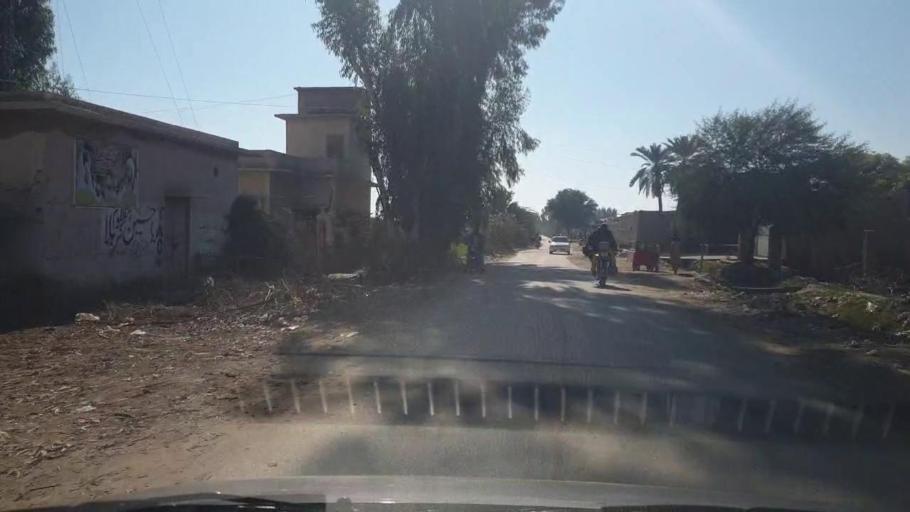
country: PK
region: Sindh
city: Bozdar
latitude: 27.1809
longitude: 68.6393
